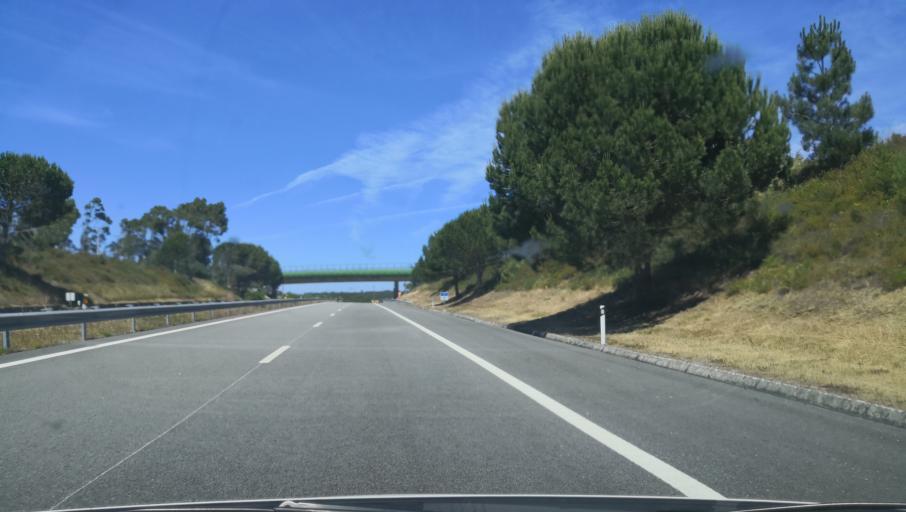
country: PT
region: Coimbra
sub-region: Montemor-O-Velho
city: Arazede
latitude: 40.2312
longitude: -8.6666
